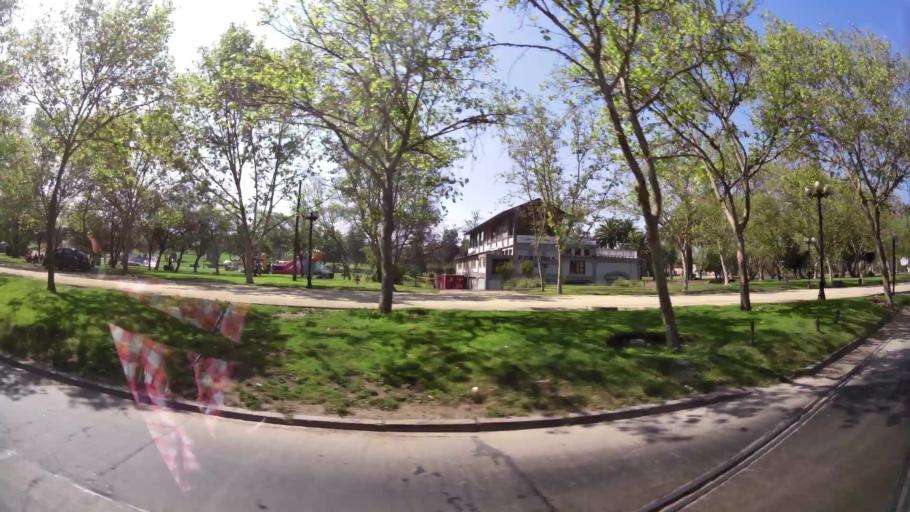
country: CL
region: Santiago Metropolitan
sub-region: Provincia de Santiago
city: Santiago
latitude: -33.4278
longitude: -70.6733
